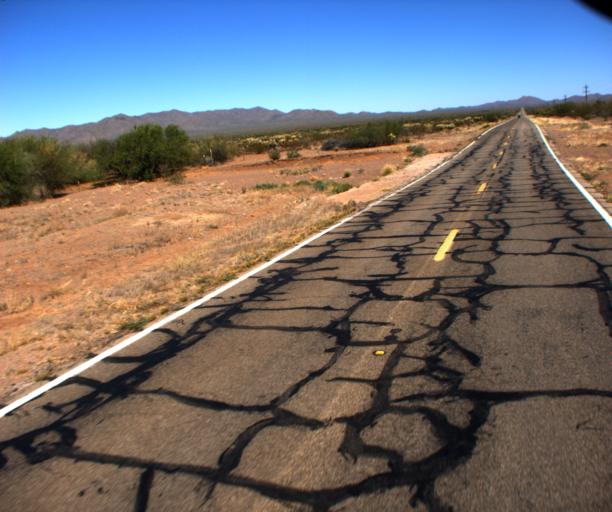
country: US
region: Arizona
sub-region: Pima County
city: Sells
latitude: 32.0796
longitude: -112.0491
